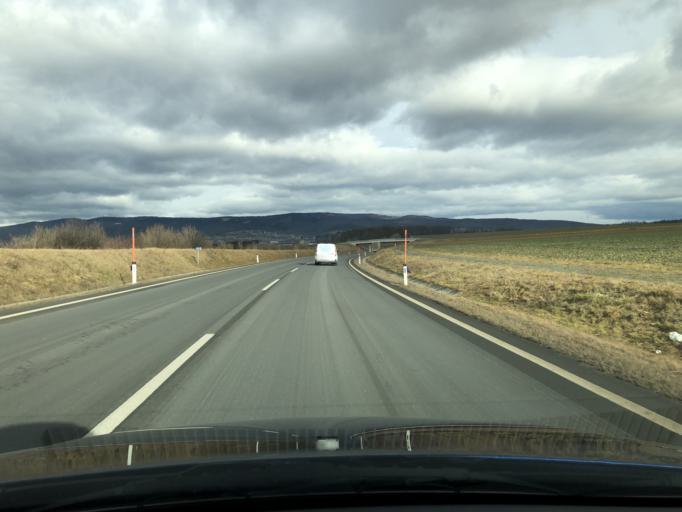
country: AT
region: Burgenland
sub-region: Politischer Bezirk Oberwart
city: Schachendorf
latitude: 47.2655
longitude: 16.4482
